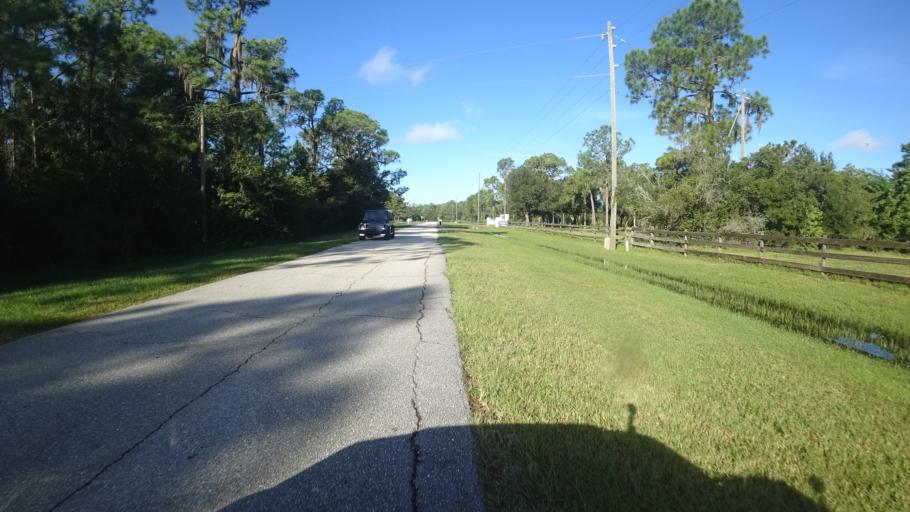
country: US
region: Florida
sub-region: Sarasota County
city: The Meadows
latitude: 27.4171
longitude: -82.3453
